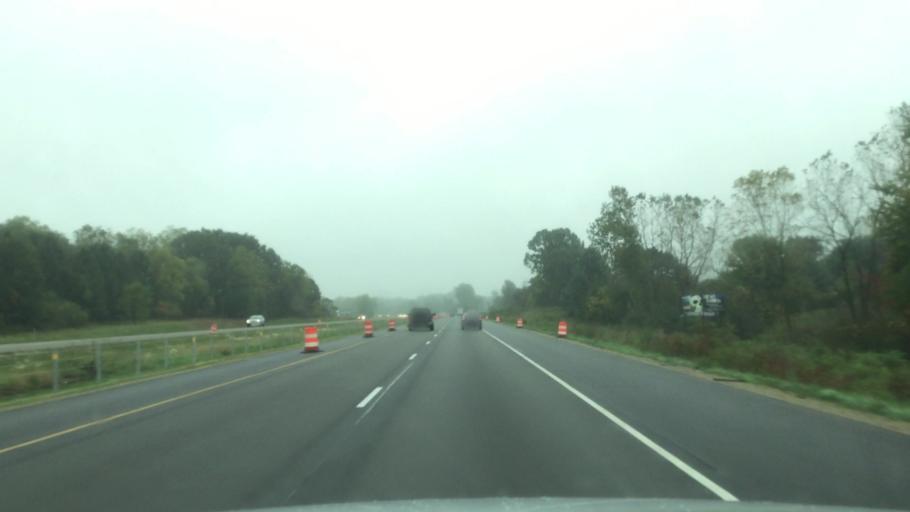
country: US
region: Michigan
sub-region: Van Buren County
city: Decatur
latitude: 42.1921
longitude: -86.0155
